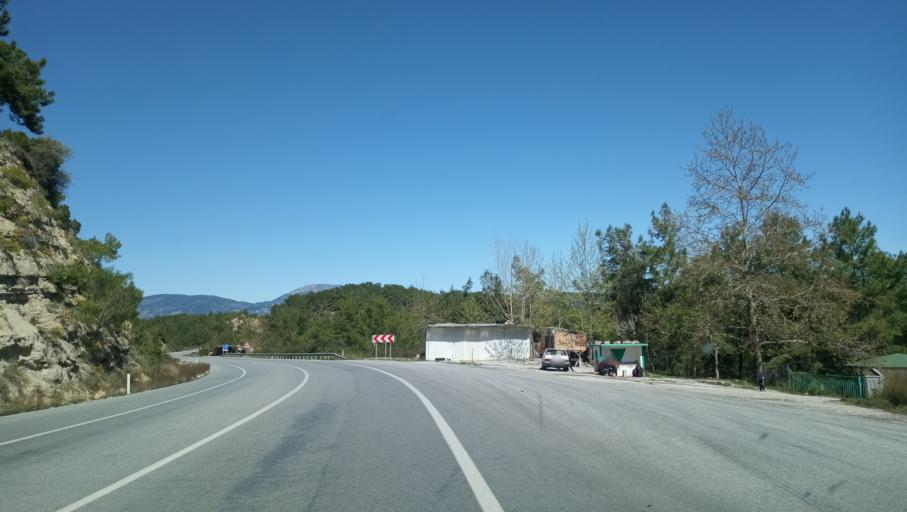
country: TR
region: Antalya
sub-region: Manavgat
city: Kizilagac
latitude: 36.7367
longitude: 31.6127
